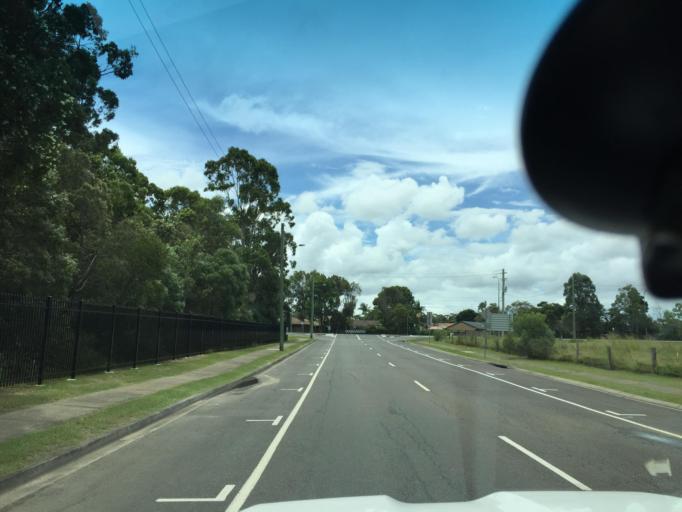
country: AU
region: Queensland
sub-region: Moreton Bay
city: Morayfield
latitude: -27.1100
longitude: 152.9249
